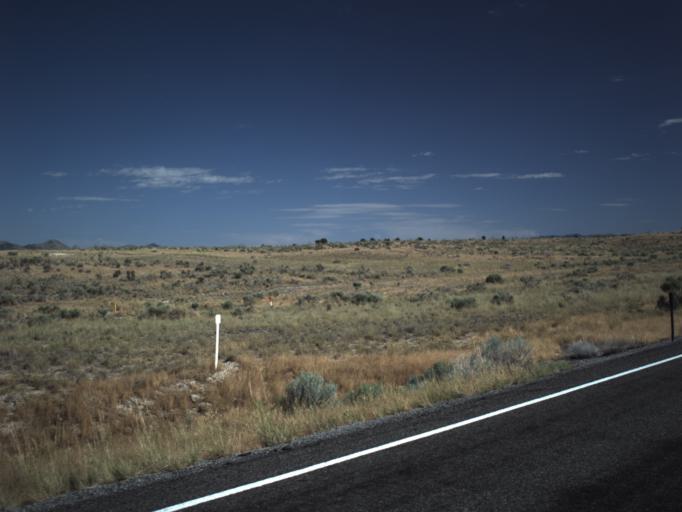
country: US
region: Utah
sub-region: Juab County
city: Mona
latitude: 39.7422
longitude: -112.1879
